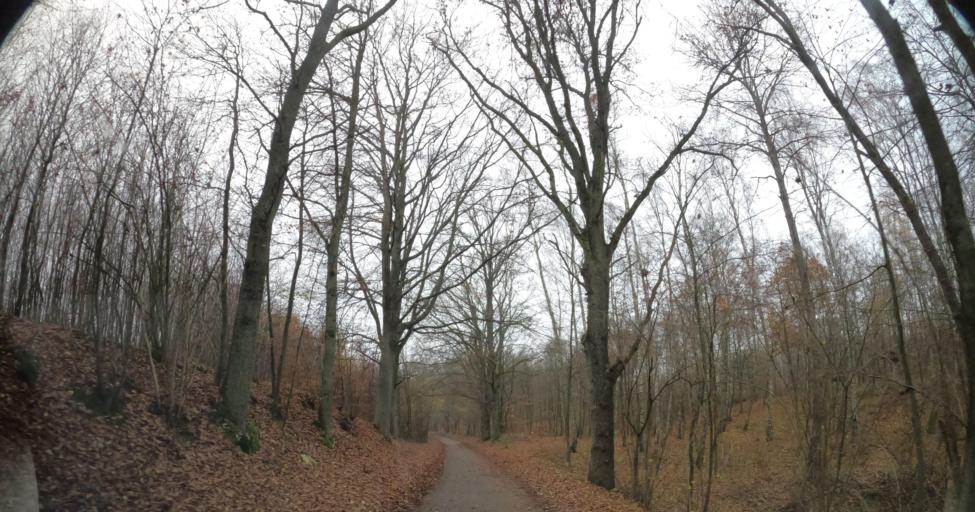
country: PL
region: West Pomeranian Voivodeship
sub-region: Powiat drawski
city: Drawsko Pomorskie
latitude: 53.5817
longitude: 15.8059
